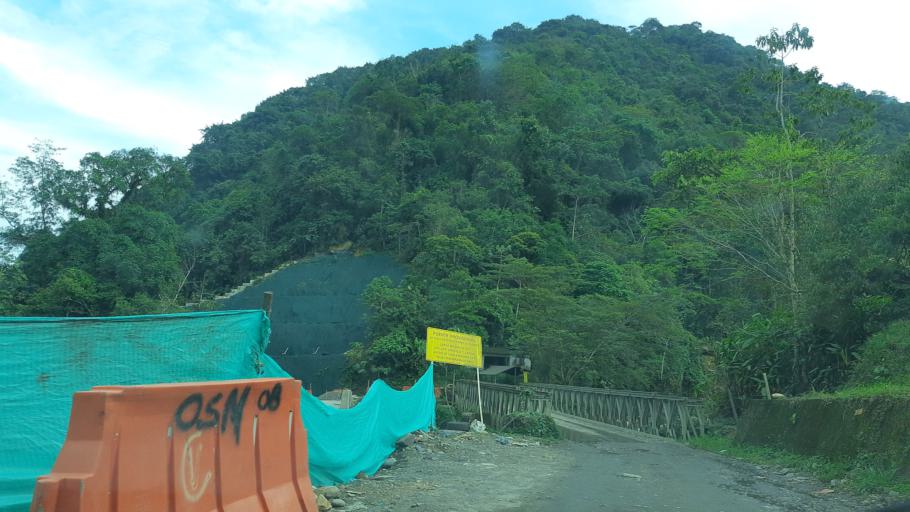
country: CO
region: Boyaca
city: Santa Maria
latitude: 4.8542
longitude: -73.2317
